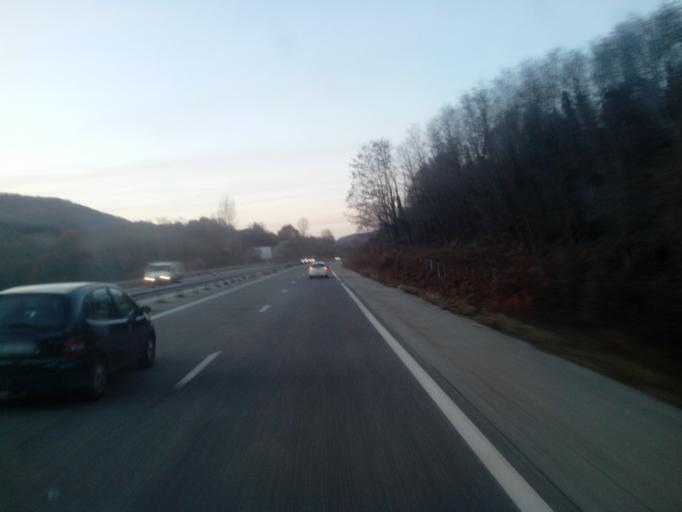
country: FR
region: Midi-Pyrenees
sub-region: Departement de l'Ariege
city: Montgaillard
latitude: 42.9310
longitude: 1.6297
